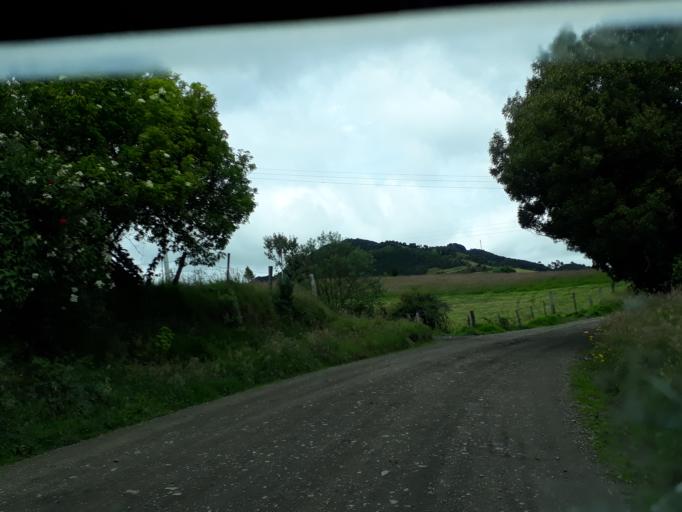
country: CO
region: Cundinamarca
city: La Mesa
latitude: 5.2088
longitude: -73.9132
